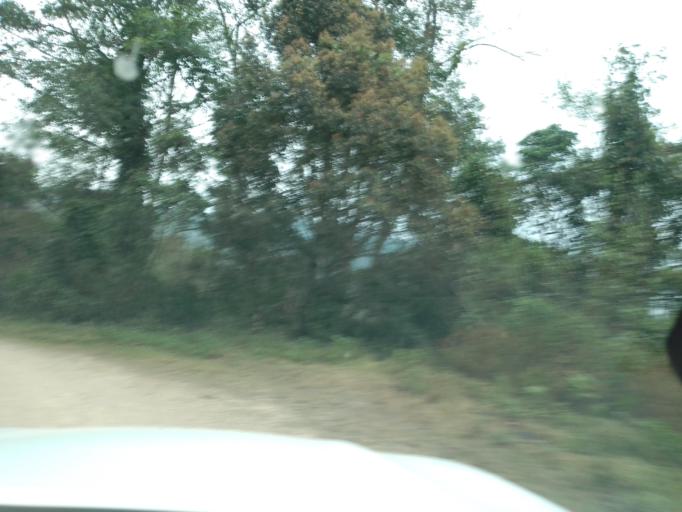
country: MX
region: Chiapas
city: Motozintla de Mendoza
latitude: 15.2189
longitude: -92.2293
